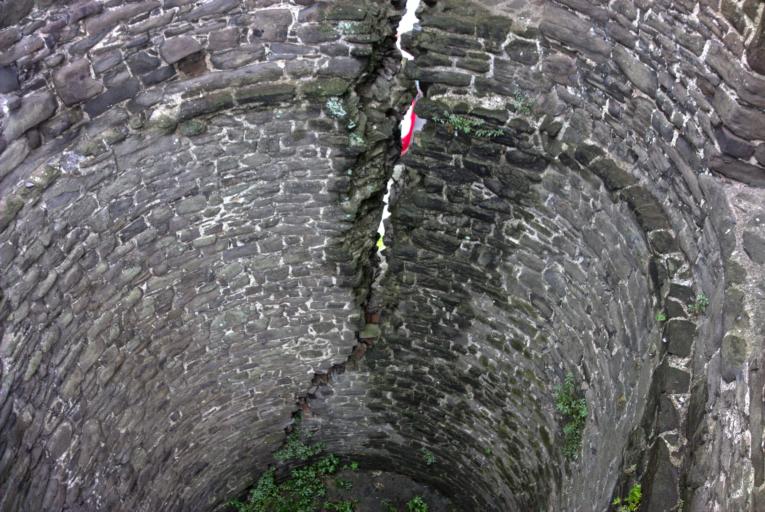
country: GB
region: Wales
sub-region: Conwy
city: Conwy
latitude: 53.2809
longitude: -3.8322
